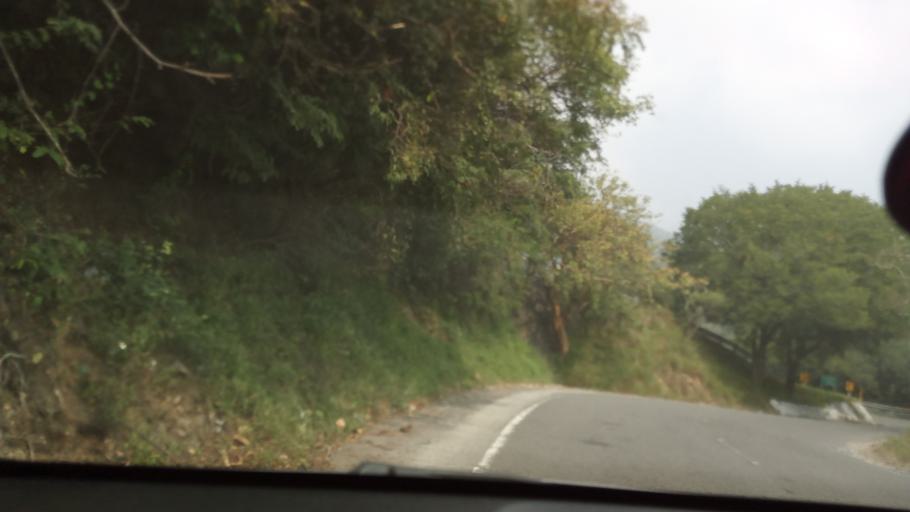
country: IN
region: Tamil Nadu
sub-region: Erode
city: Sathyamangalam
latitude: 11.5944
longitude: 77.1271
